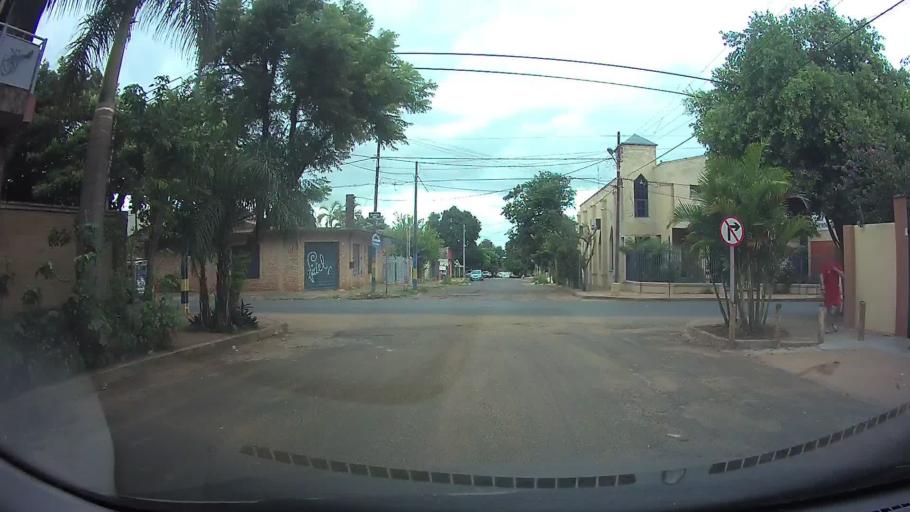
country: PY
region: Central
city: San Lorenzo
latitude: -25.2694
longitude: -57.4804
